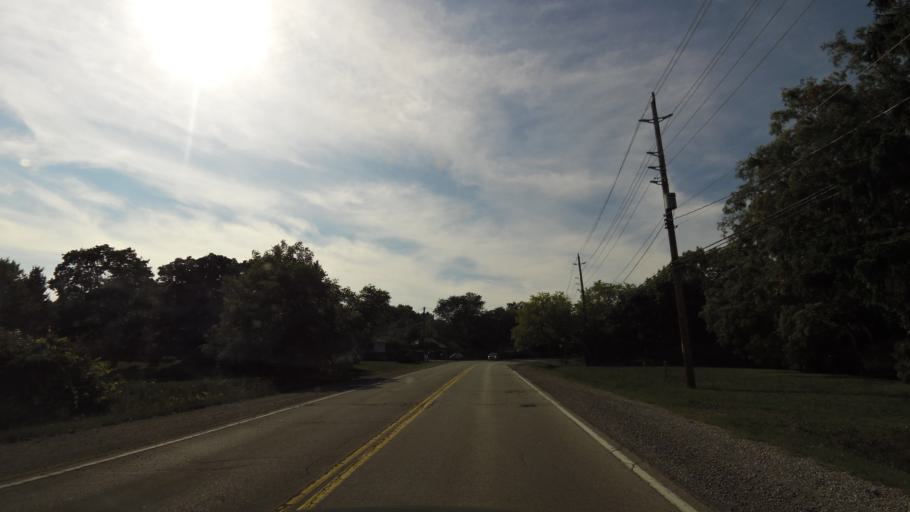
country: CA
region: Ontario
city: Burlington
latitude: 43.3219
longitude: -79.8752
